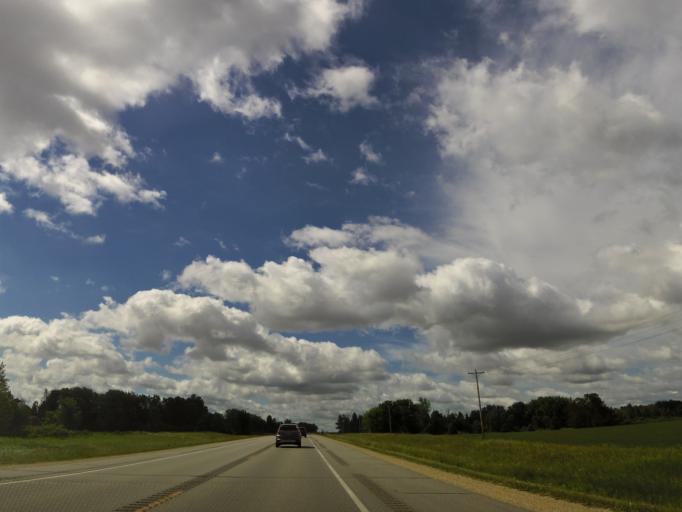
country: US
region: Minnesota
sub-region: Olmsted County
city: Stewartville
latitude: 43.8229
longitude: -92.4892
